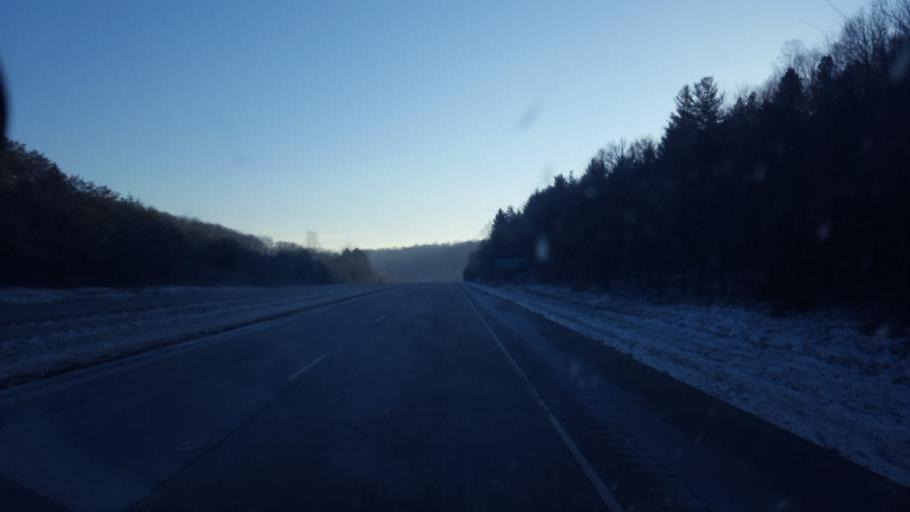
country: US
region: Ohio
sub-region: Pike County
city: Piketon
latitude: 39.0608
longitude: -83.1054
